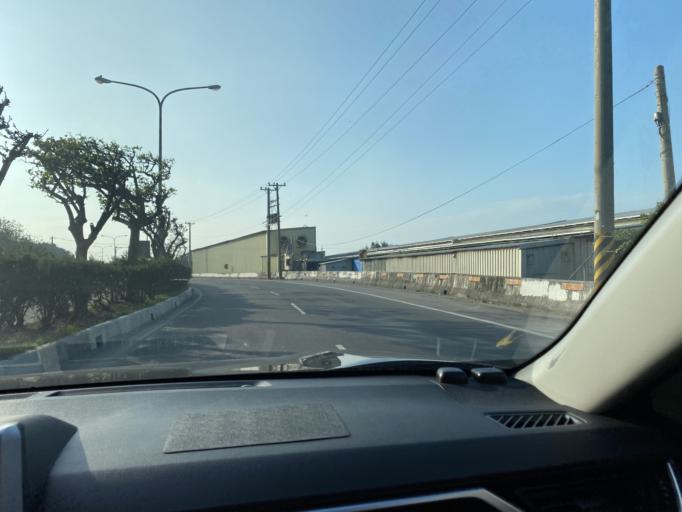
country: TW
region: Taiwan
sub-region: Changhua
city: Chang-hua
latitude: 23.9618
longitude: 120.3555
